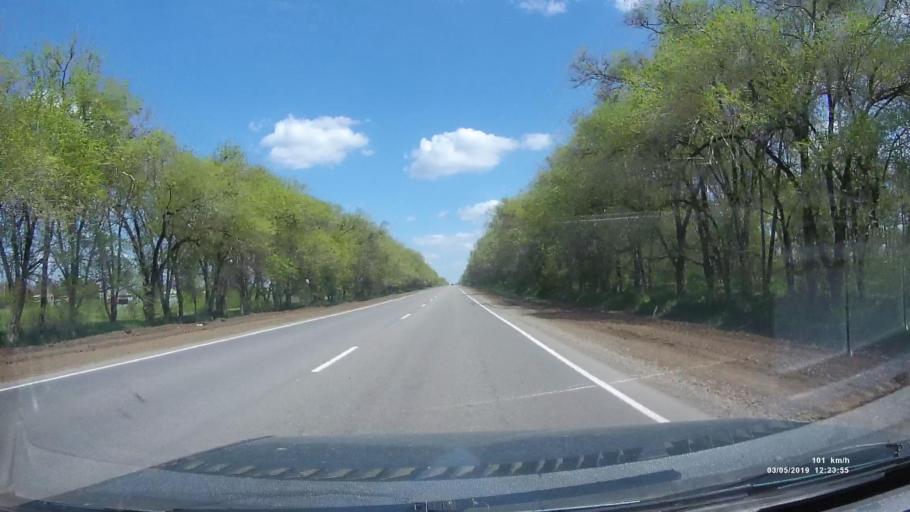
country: RU
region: Rostov
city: Semikarakorsk
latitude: 47.4144
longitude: 40.6910
